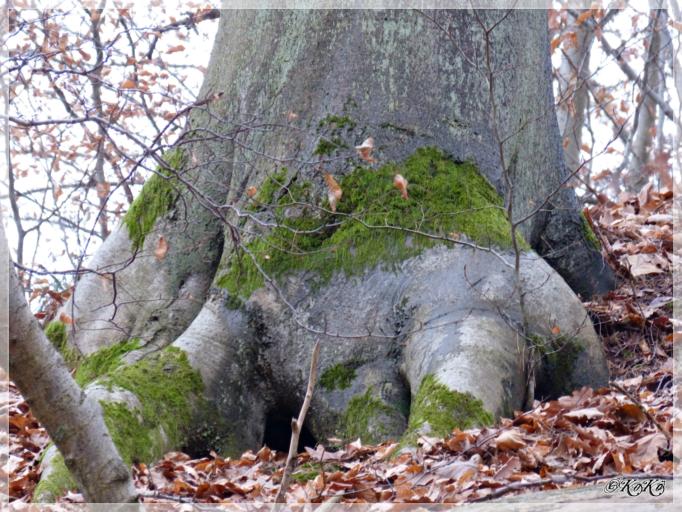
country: DE
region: Saarland
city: Bexbach
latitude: 49.3391
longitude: 7.2196
